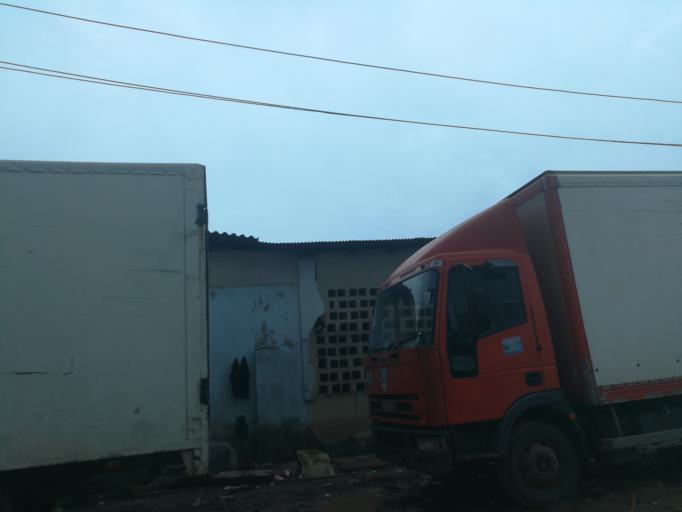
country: NG
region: Lagos
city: Agege
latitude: 6.6129
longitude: 3.3320
